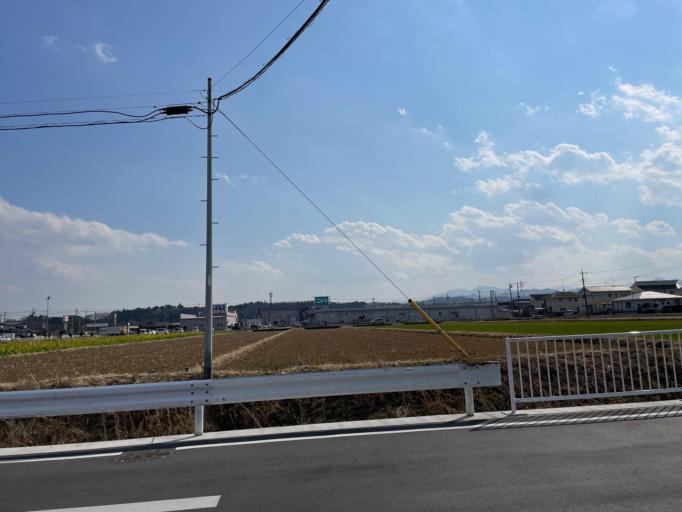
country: JP
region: Saitama
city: Yorii
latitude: 36.1233
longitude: 139.2337
